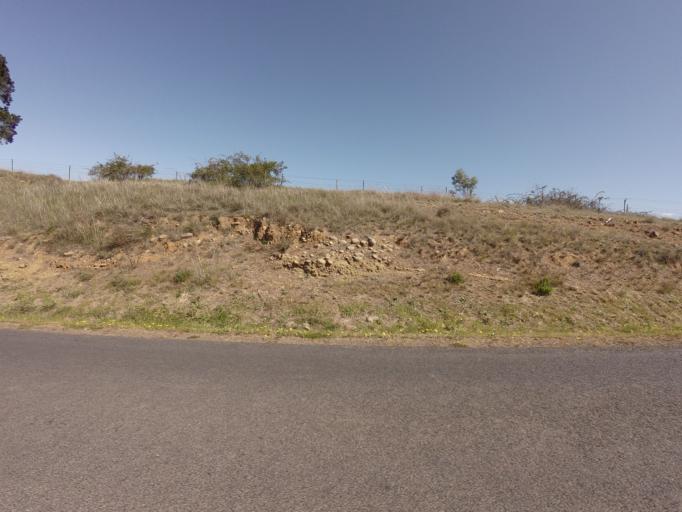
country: AU
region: Tasmania
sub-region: Derwent Valley
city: New Norfolk
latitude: -42.5369
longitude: 146.7313
